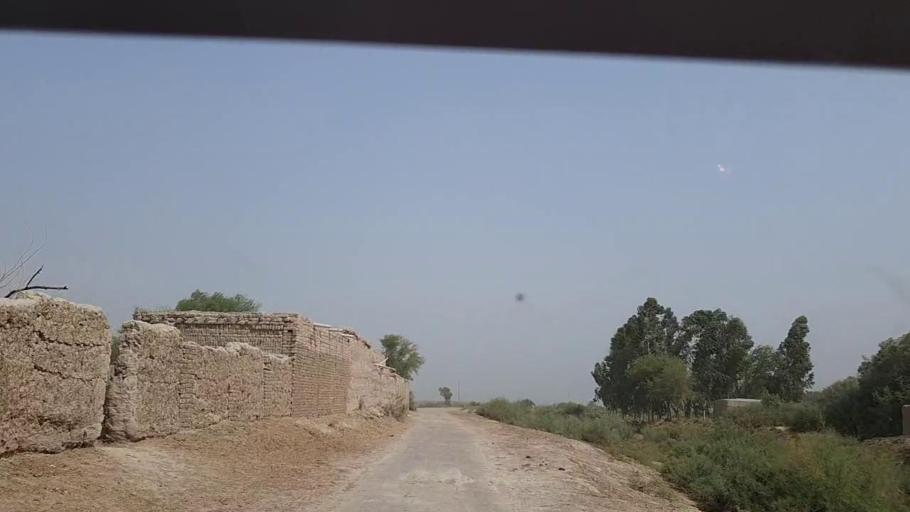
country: PK
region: Sindh
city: Khairpur Nathan Shah
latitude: 27.0461
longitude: 67.6849
